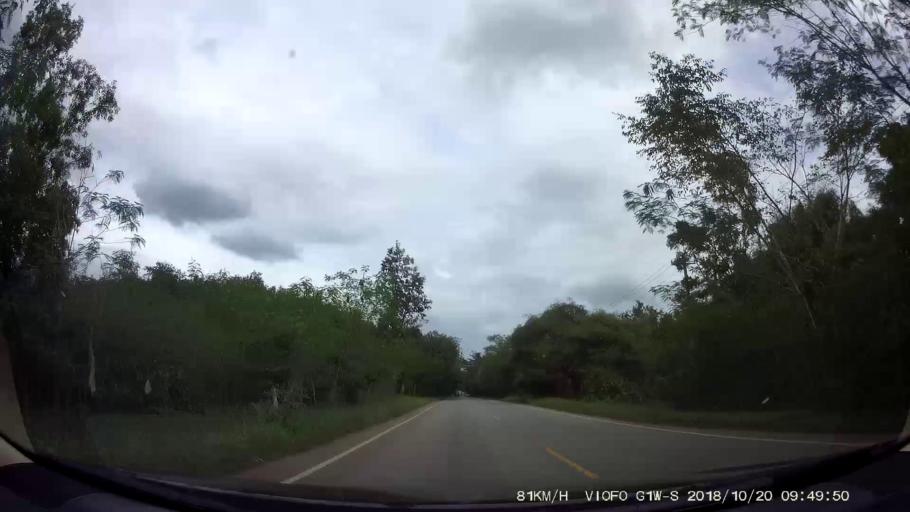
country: TH
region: Chaiyaphum
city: Khon San
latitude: 16.5243
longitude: 101.9039
